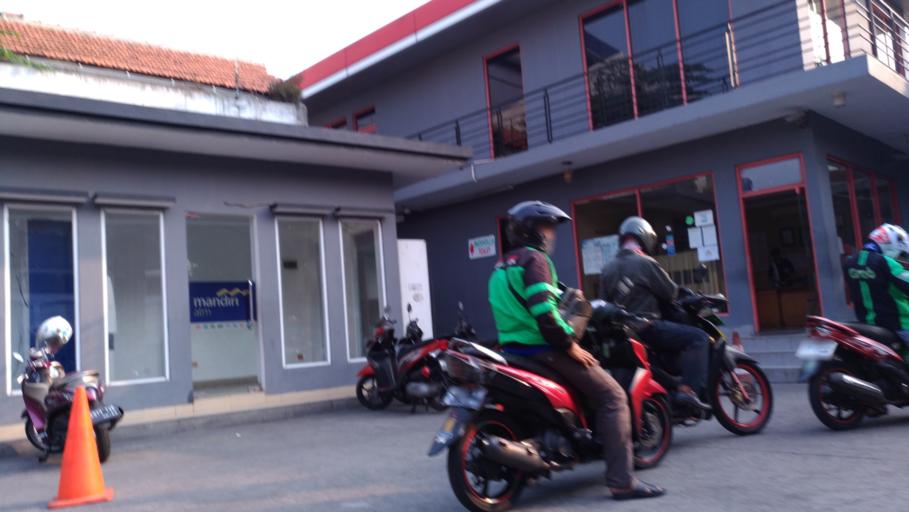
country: ID
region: Jakarta Raya
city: Jakarta
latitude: -6.2197
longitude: 106.8674
